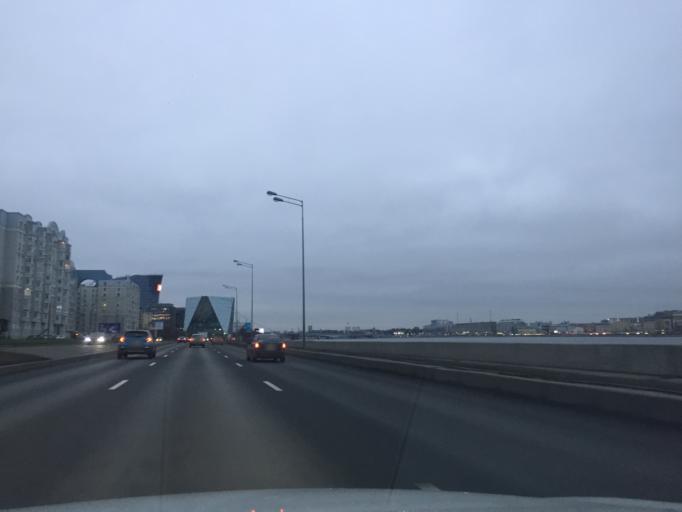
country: RU
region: St.-Petersburg
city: Centralniy
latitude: 59.9394
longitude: 30.4036
